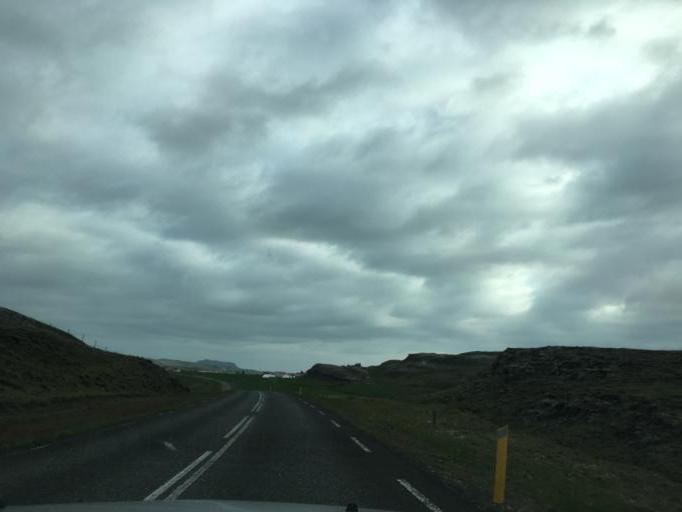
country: IS
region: South
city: Vestmannaeyjar
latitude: 64.2045
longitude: -20.2739
